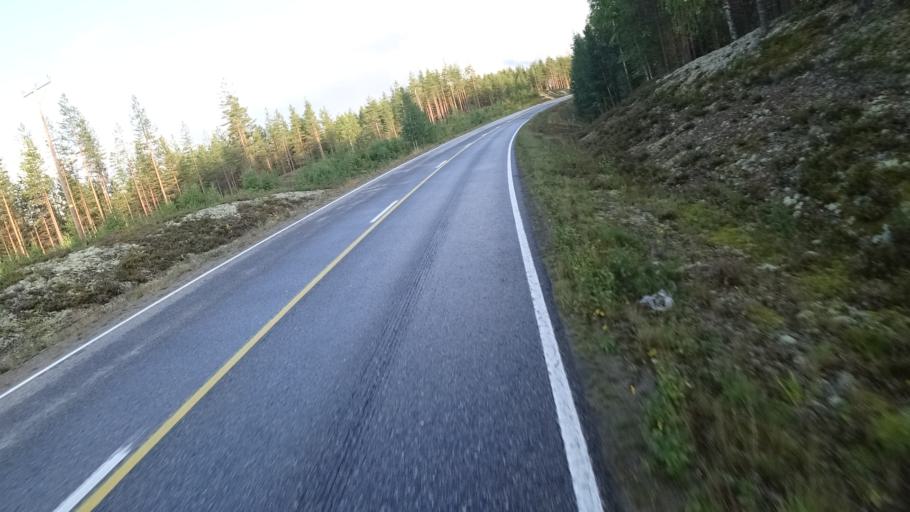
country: FI
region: North Karelia
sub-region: Joensuu
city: Ilomantsi
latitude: 62.6349
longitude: 31.0914
